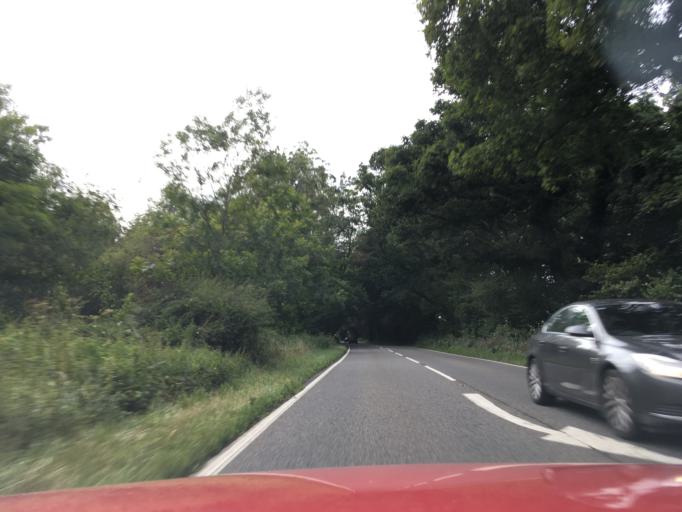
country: GB
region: England
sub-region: Hampshire
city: Four Marks
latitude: 51.0377
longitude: -1.0972
